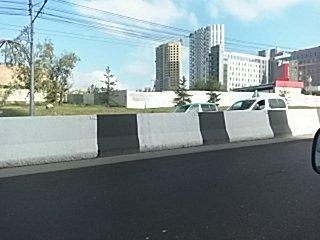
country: RU
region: Krasnoyarskiy
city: Krasnoyarsk
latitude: 56.0336
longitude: 92.9239
